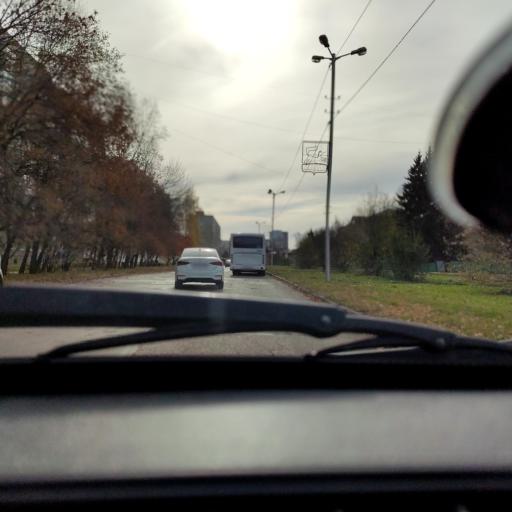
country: RU
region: Bashkortostan
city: Mikhaylovka
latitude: 54.7117
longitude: 55.8268
